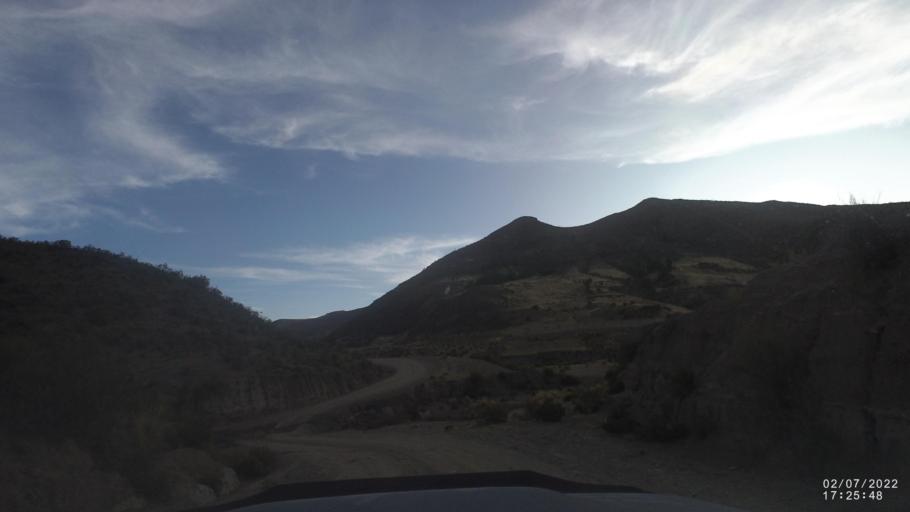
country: BO
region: Cochabamba
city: Irpa Irpa
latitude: -17.8780
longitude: -66.6087
